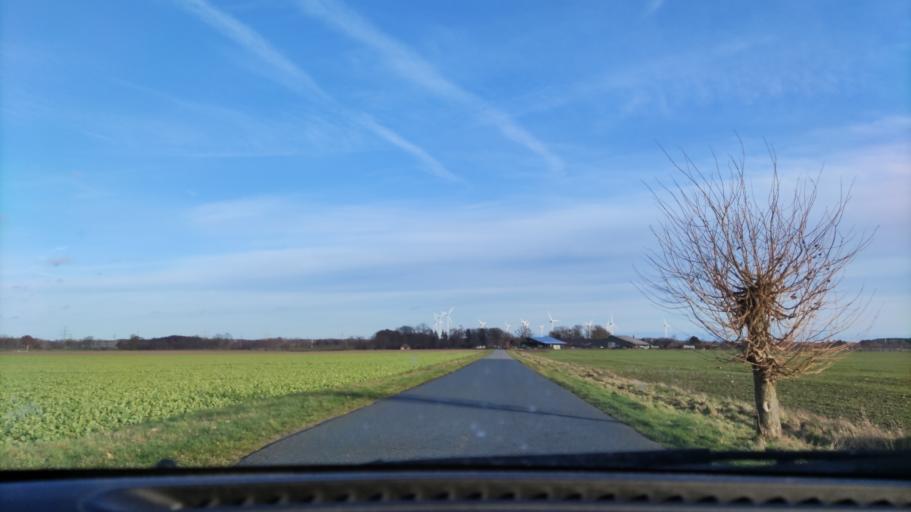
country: DE
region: Lower Saxony
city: Eimke
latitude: 52.9819
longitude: 10.3564
